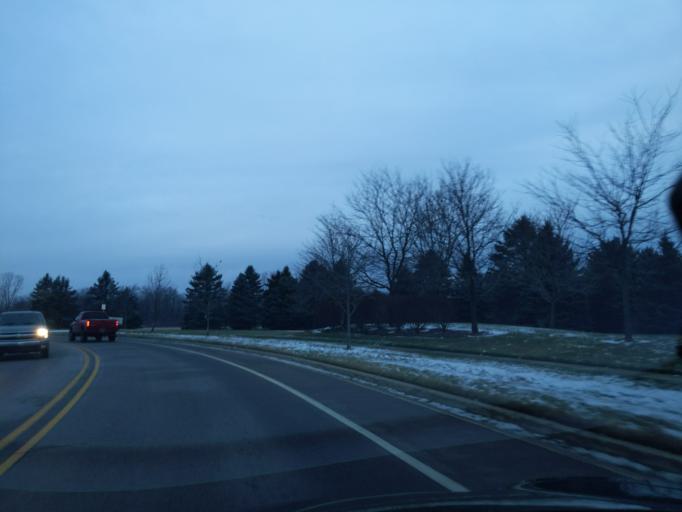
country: US
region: Michigan
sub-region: Ingham County
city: Mason
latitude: 42.5694
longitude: -84.4452
